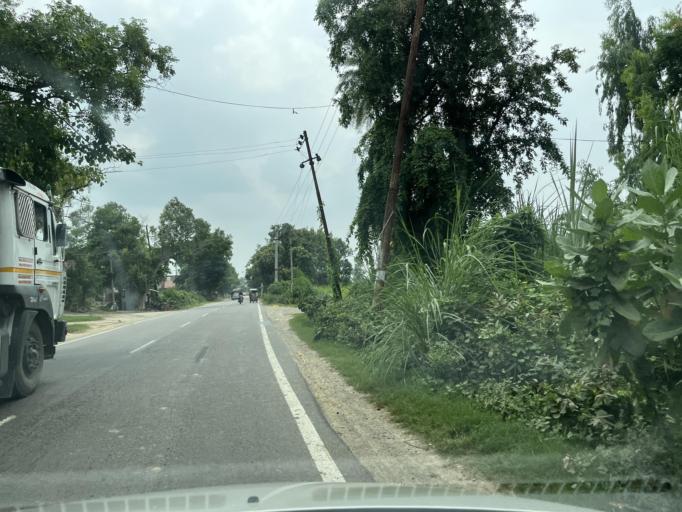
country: IN
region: Uttar Pradesh
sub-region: Bijnor
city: Najibabad
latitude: 29.5870
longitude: 78.3387
